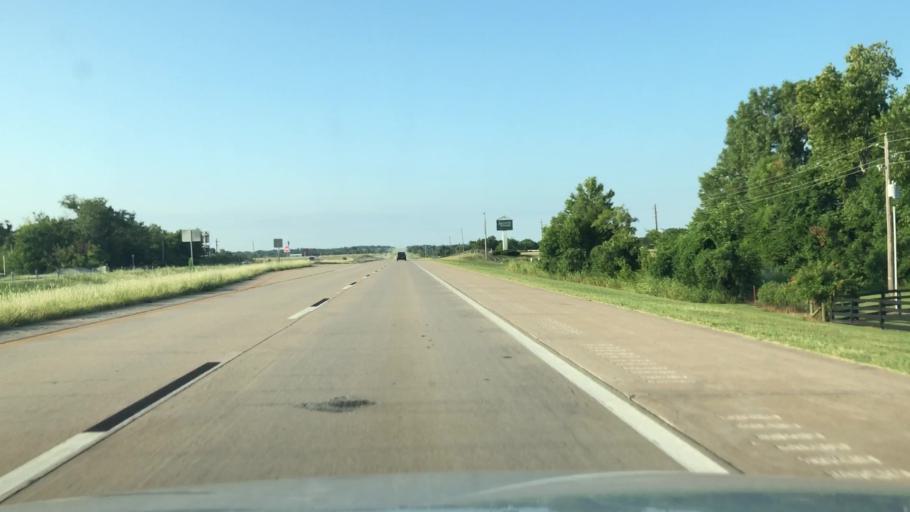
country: US
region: Oklahoma
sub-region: Osage County
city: Skiatook
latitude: 36.4609
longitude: -95.9207
